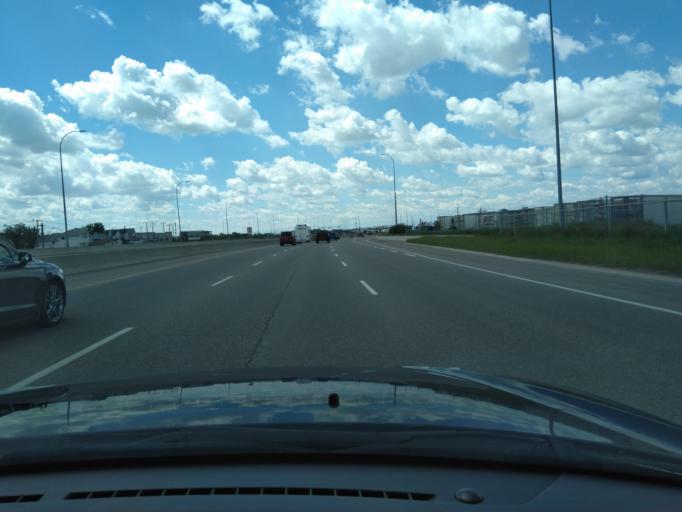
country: CA
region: Alberta
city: Calgary
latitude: 51.1150
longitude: -113.9716
